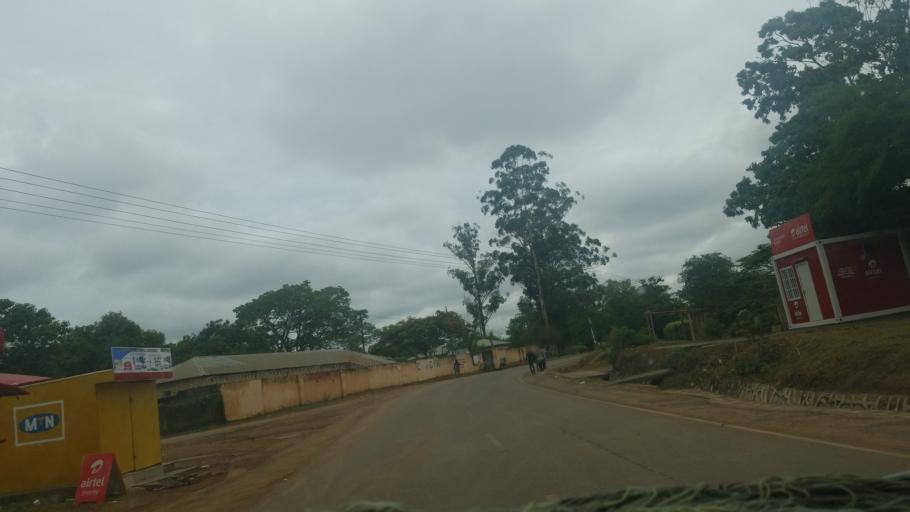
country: ZM
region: Luapula
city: Mansa
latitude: -11.1973
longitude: 28.8916
